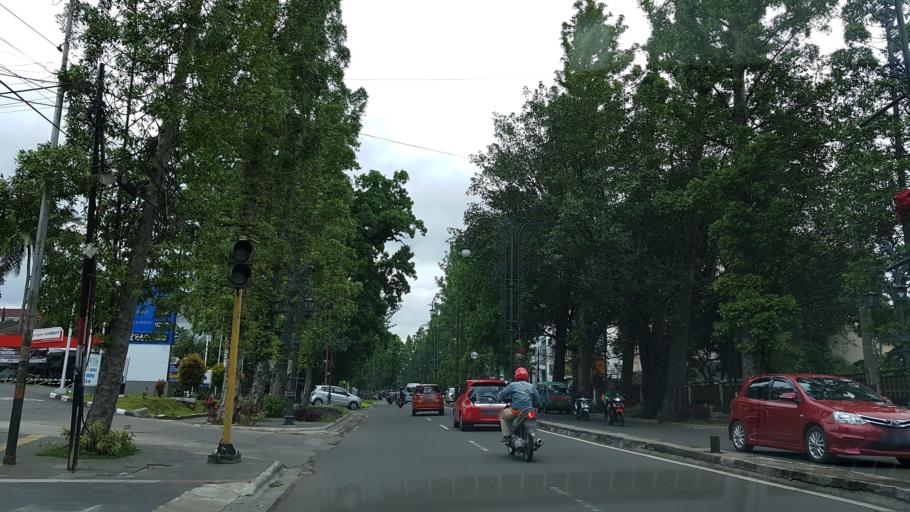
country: ID
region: West Java
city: Bandung
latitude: -6.8905
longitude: 107.6133
